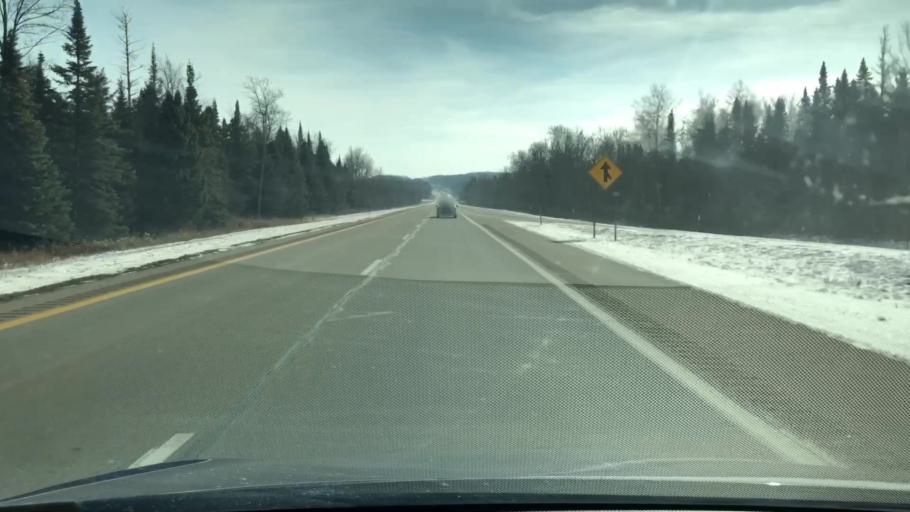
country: US
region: Michigan
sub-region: Roscommon County
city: Roscommon
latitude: 44.5076
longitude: -84.6590
